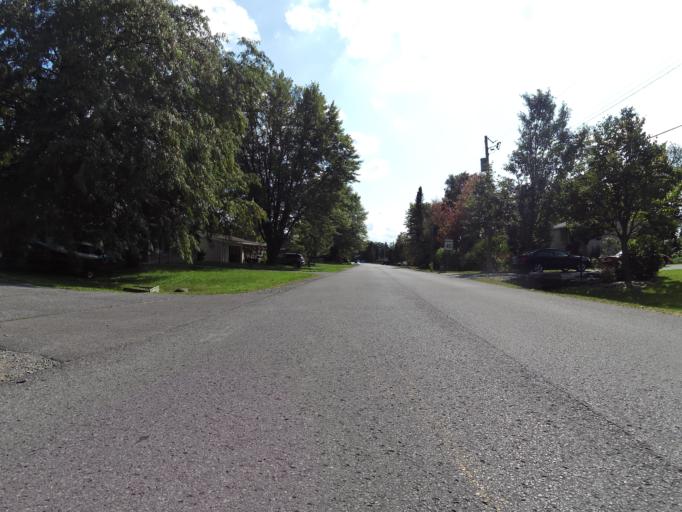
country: CA
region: Ontario
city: Bells Corners
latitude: 45.2401
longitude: -75.7011
